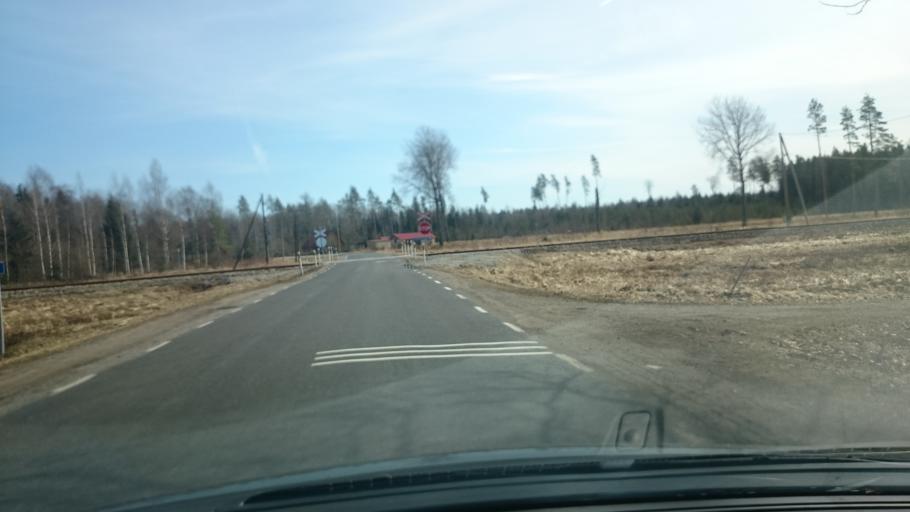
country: EE
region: Paernumaa
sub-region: Tootsi vald
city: Tootsi
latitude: 58.6454
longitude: 24.8675
